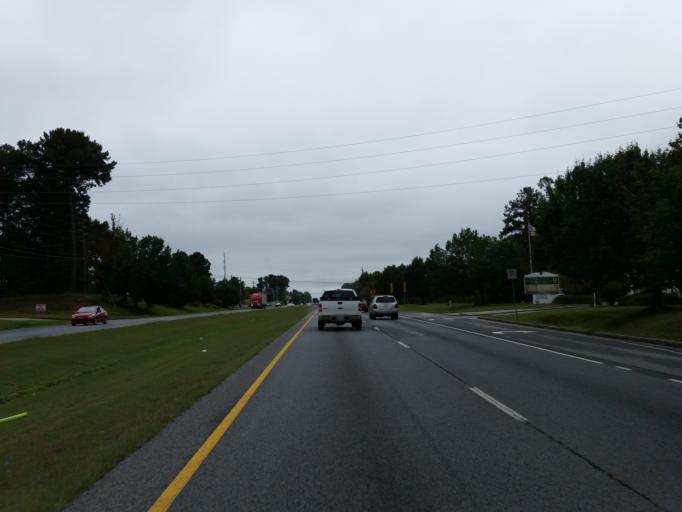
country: US
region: Georgia
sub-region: Clayton County
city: Irondale
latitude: 33.4897
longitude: -84.3415
